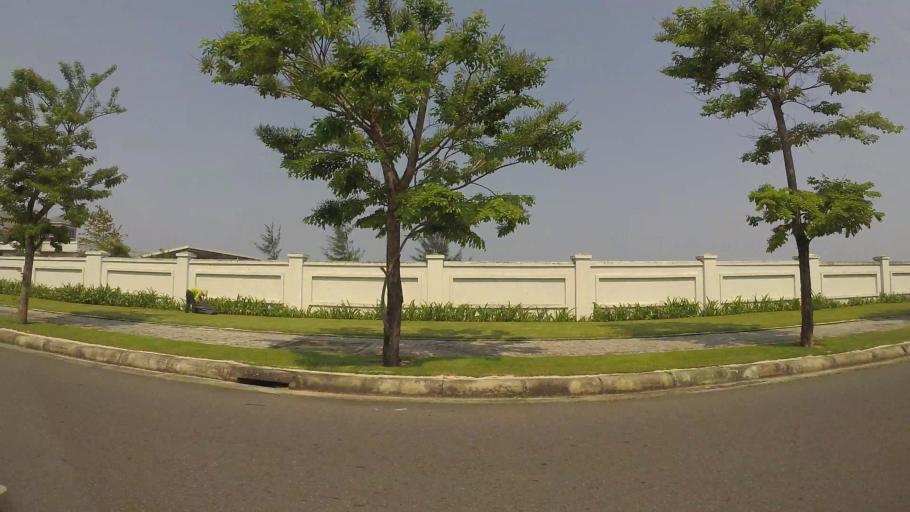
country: VN
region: Da Nang
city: Ngu Hanh Son
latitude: 15.9931
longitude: 108.2692
